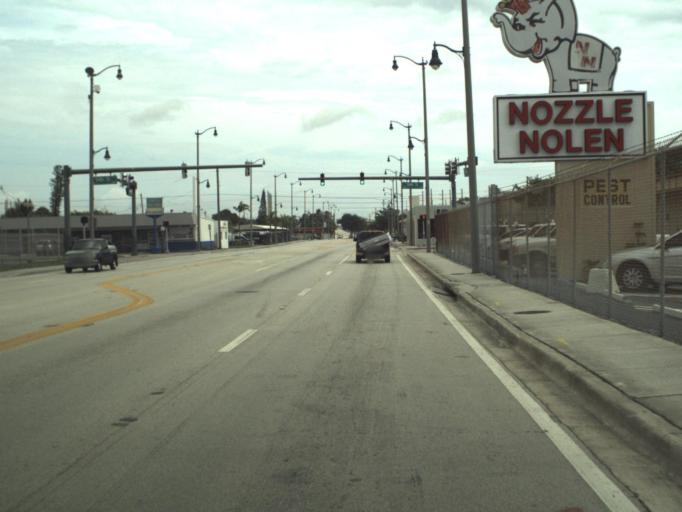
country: US
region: Florida
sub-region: Palm Beach County
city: Riviera Beach
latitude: 26.7589
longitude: -80.0555
